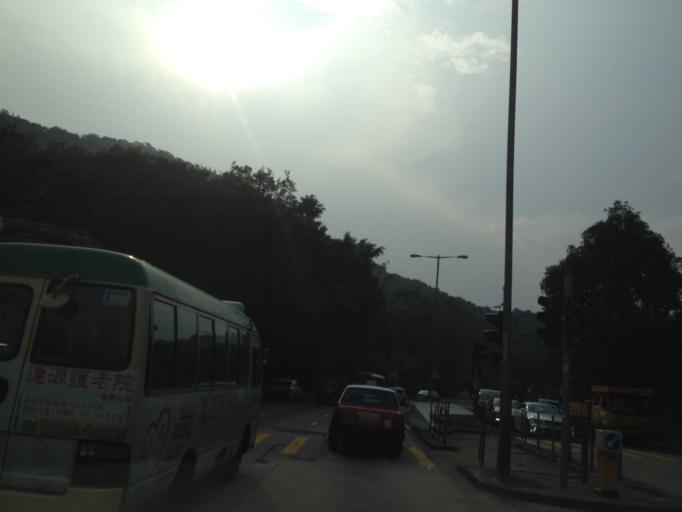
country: HK
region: Wanchai
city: Wan Chai
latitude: 22.2734
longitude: 114.2315
